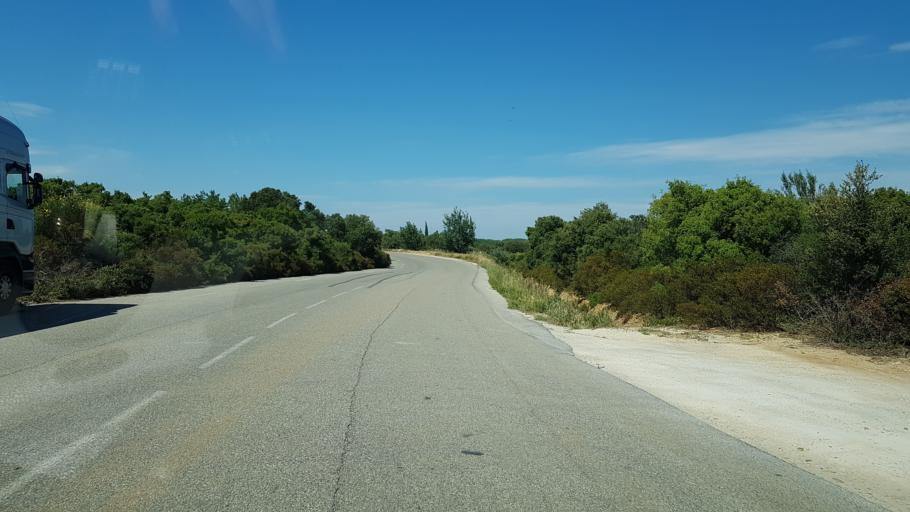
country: FR
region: Provence-Alpes-Cote d'Azur
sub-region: Departement des Bouches-du-Rhone
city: Saint-Martin-de-Crau
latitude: 43.6320
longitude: 4.7804
